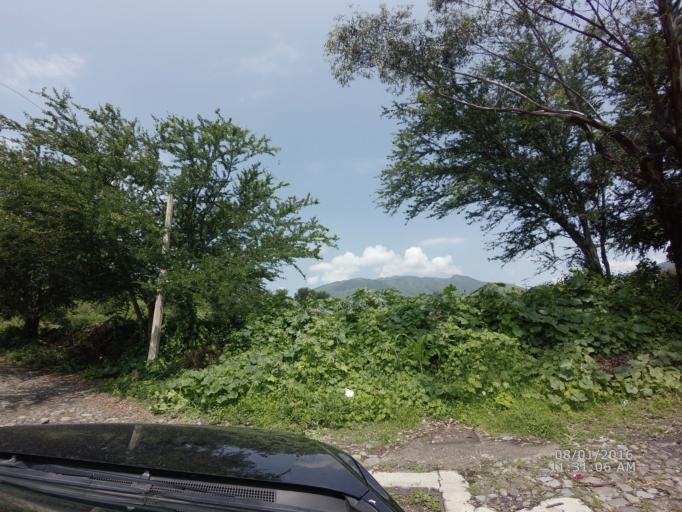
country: MX
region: Nayarit
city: Jala
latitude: 21.1089
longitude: -104.4491
